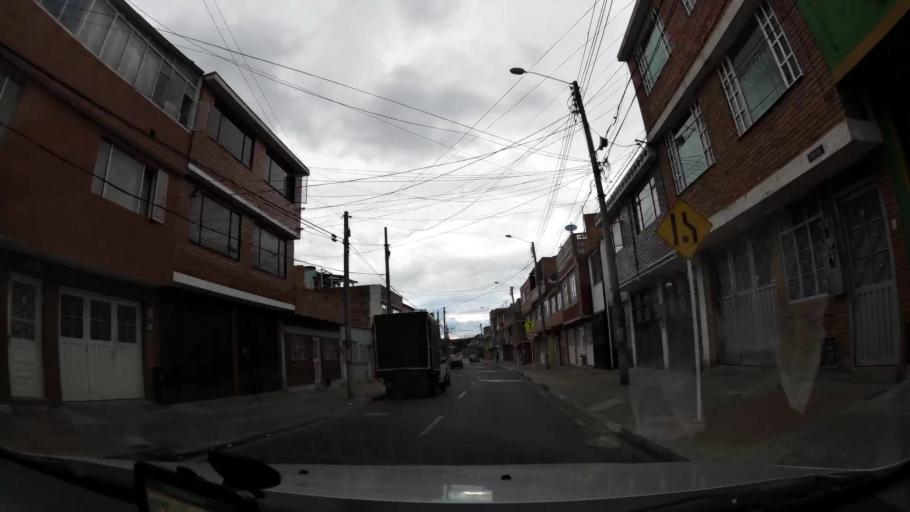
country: CO
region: Bogota D.C.
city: Bogota
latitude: 4.5934
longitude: -74.1430
